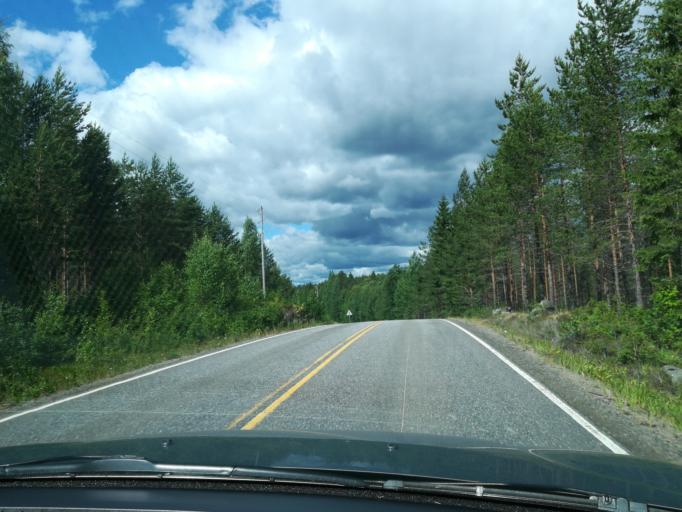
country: FI
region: Southern Savonia
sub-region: Mikkeli
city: Maentyharju
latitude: 61.3626
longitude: 27.0578
